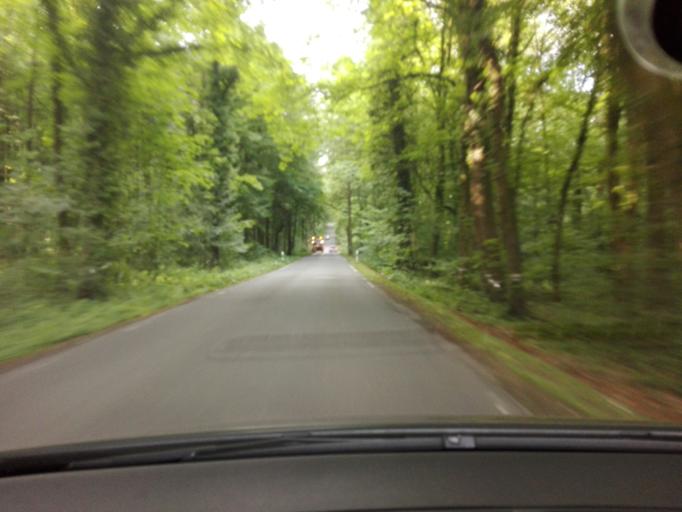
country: DE
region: North Rhine-Westphalia
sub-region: Regierungsbezirk Arnsberg
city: Frondenberg
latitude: 51.4964
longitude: 7.7506
